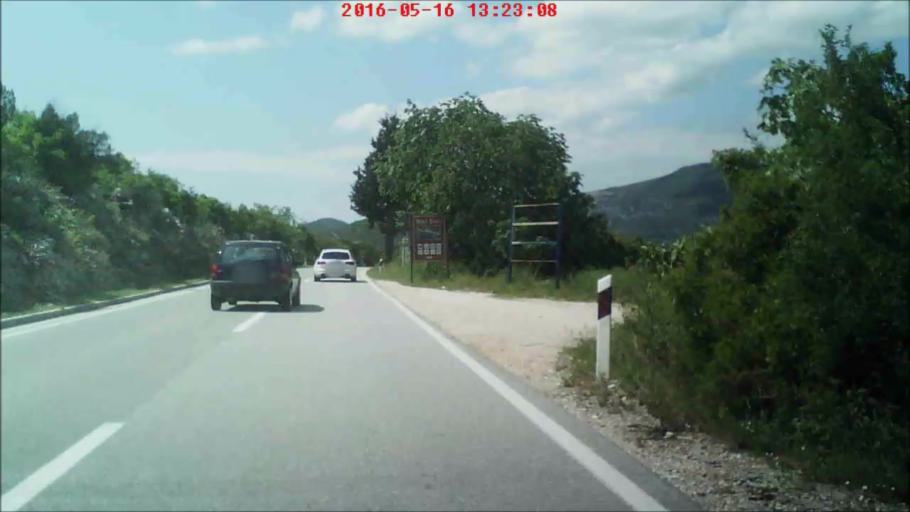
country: HR
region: Dubrovacko-Neretvanska
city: Ston
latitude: 42.8398
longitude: 17.7160
